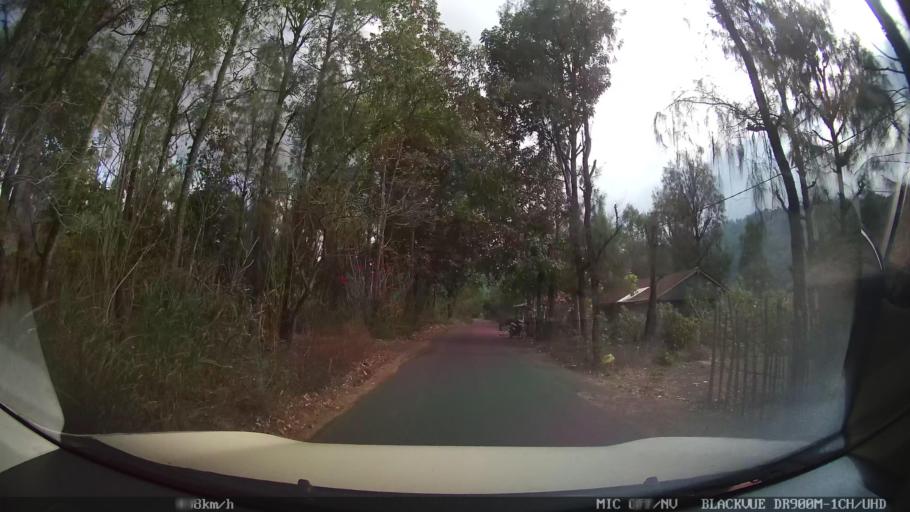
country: ID
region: Bali
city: Banjar Kedisan
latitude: -8.2338
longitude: 115.3562
